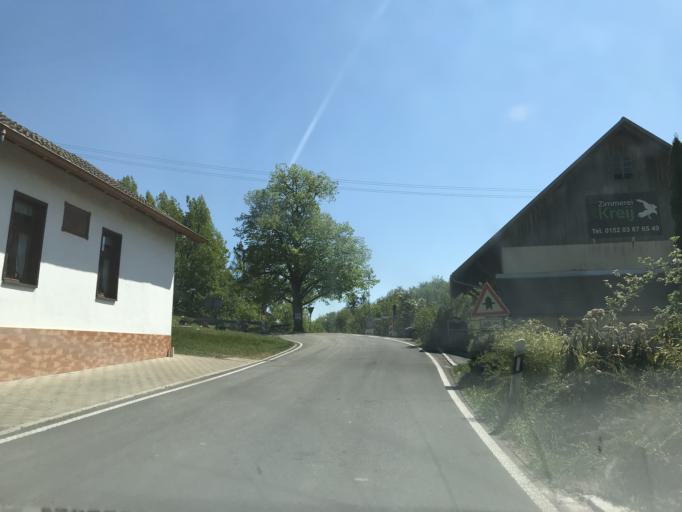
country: DE
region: Baden-Wuerttemberg
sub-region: Freiburg Region
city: Hausen
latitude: 47.6805
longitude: 7.8681
